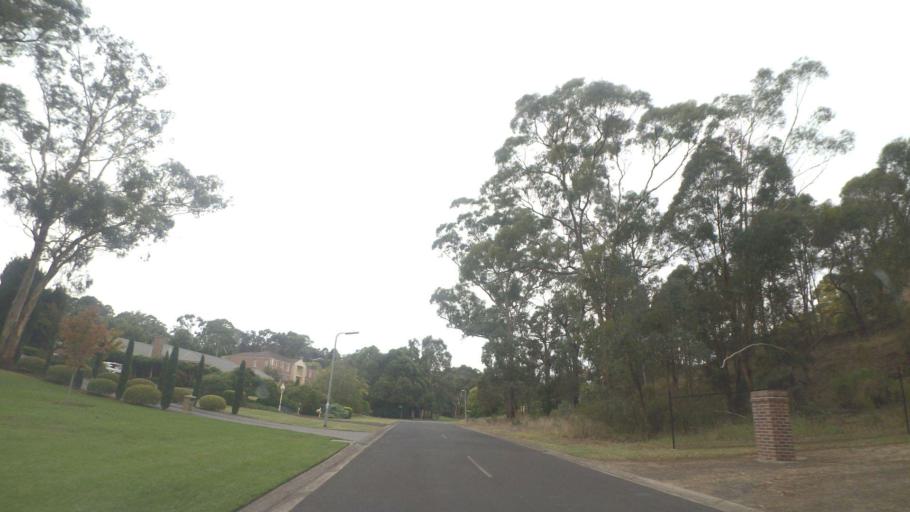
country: AU
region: Victoria
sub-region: Nillumbik
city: North Warrandyte
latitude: -37.7514
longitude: 145.1875
